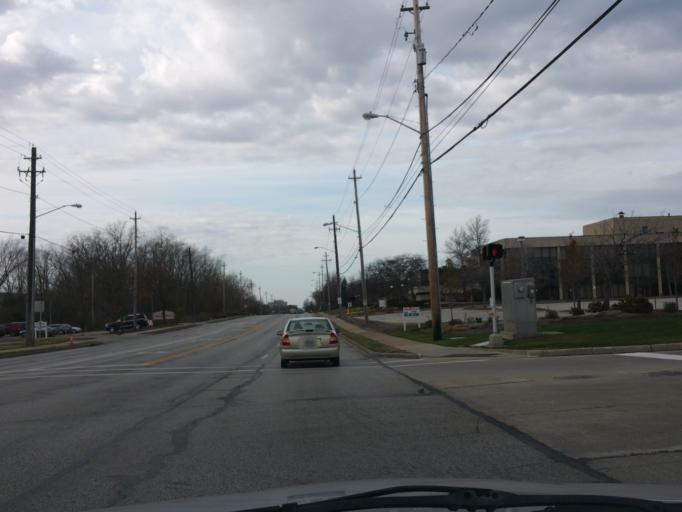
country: US
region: Ohio
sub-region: Cuyahoga County
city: Beachwood
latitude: 41.4646
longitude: -81.5085
